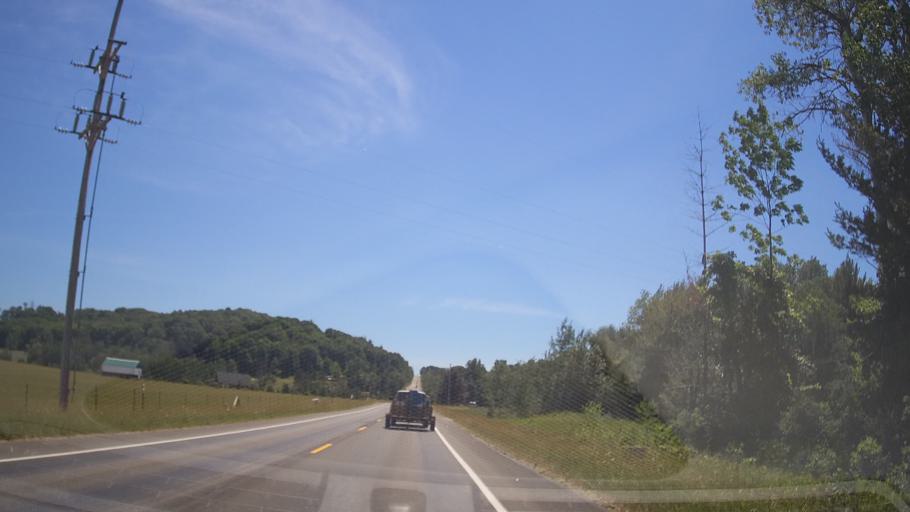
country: US
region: Michigan
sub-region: Grand Traverse County
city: Traverse City
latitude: 44.6309
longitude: -85.6964
